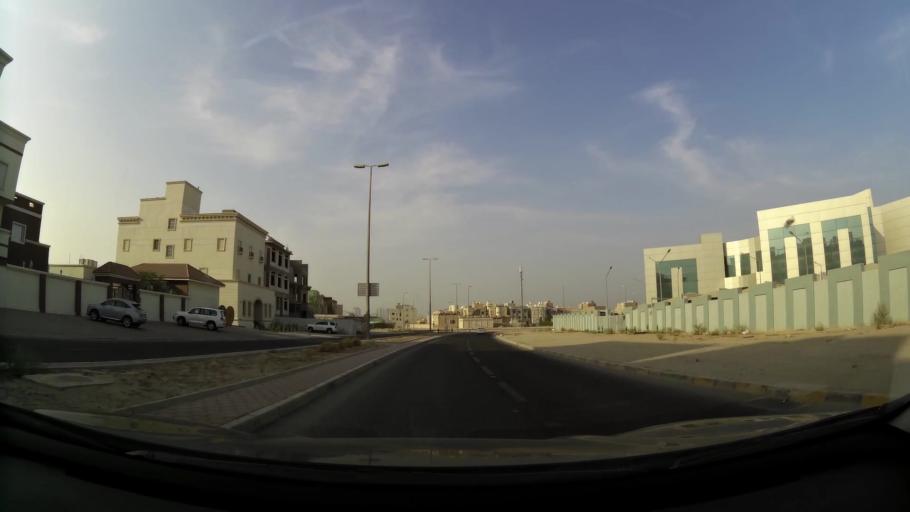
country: KW
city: Al Funaytis
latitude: 29.2294
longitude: 48.0901
